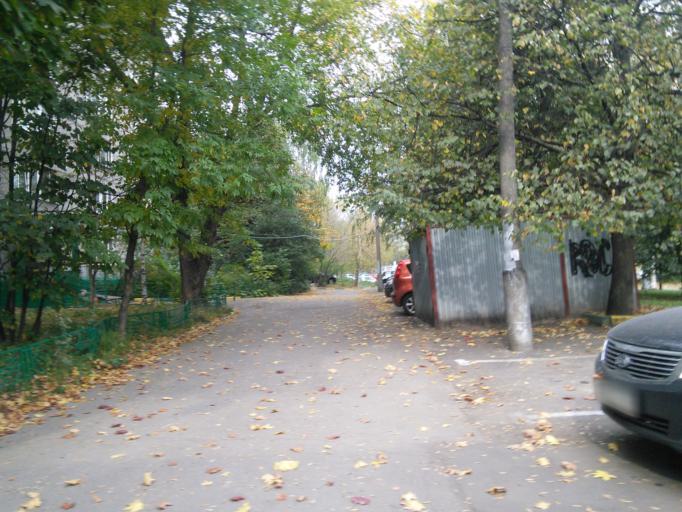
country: RU
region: Moskovskaya
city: Levoberezhnyy
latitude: 55.8615
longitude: 37.4737
